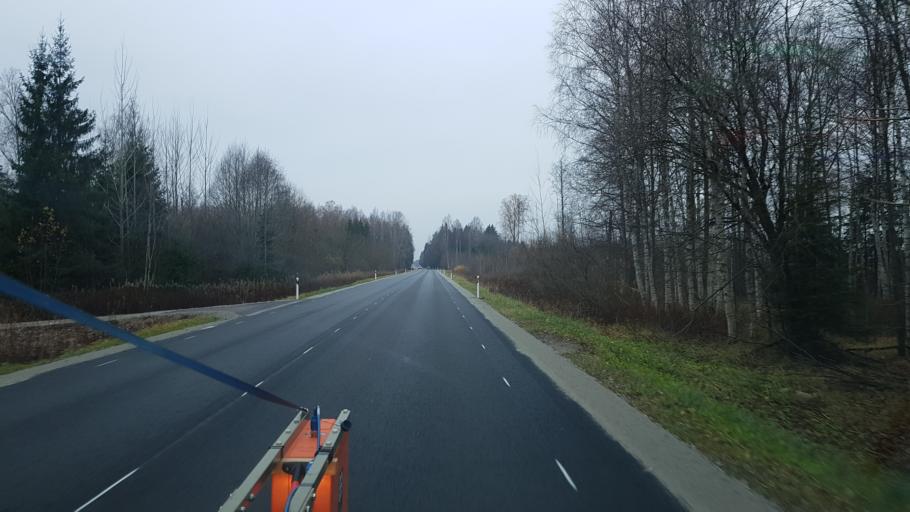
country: EE
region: Raplamaa
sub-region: Kehtna vald
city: Kehtna
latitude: 58.8439
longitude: 25.0527
